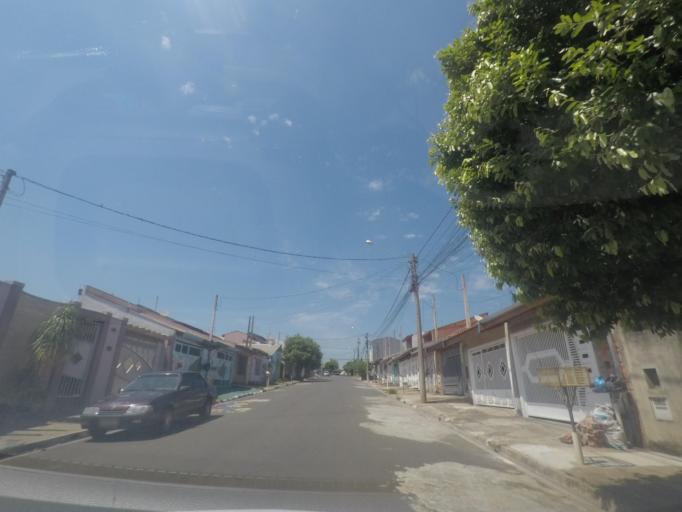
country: BR
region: Sao Paulo
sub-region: Sumare
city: Sumare
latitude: -22.8005
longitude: -47.2678
